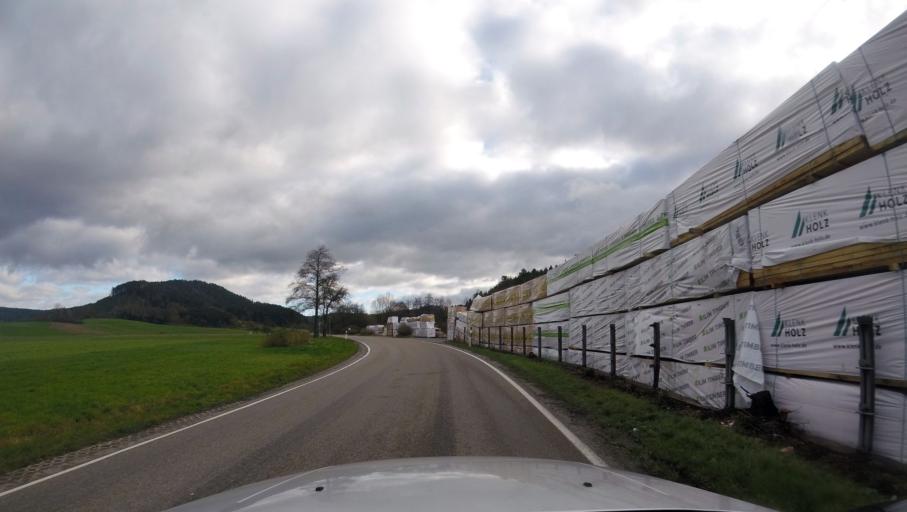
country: DE
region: Baden-Wuerttemberg
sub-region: Regierungsbezirk Stuttgart
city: Kaisersbach
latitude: 48.9704
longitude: 9.6339
